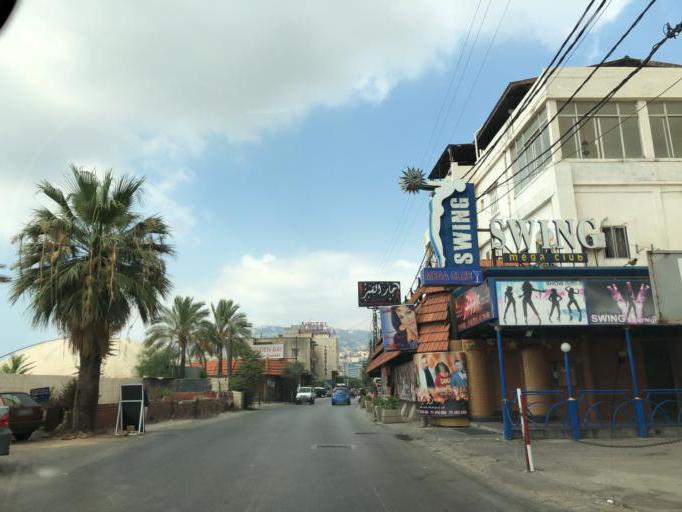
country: LB
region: Mont-Liban
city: Djounie
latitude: 33.9925
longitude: 35.6397
